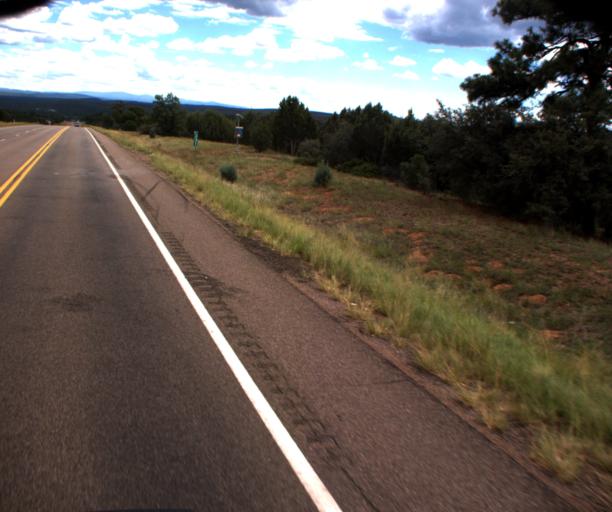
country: US
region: Arizona
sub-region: Navajo County
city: Linden
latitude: 34.2953
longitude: -110.1872
